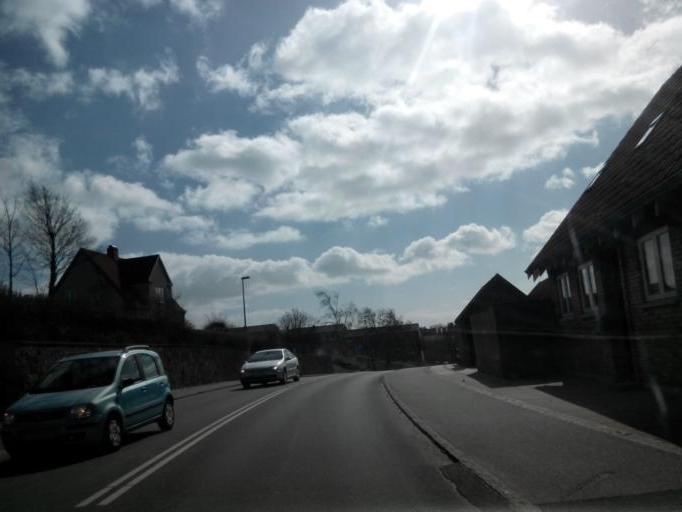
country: DK
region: Central Jutland
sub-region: Syddjurs Kommune
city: Ebeltoft
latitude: 56.2005
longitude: 10.6816
